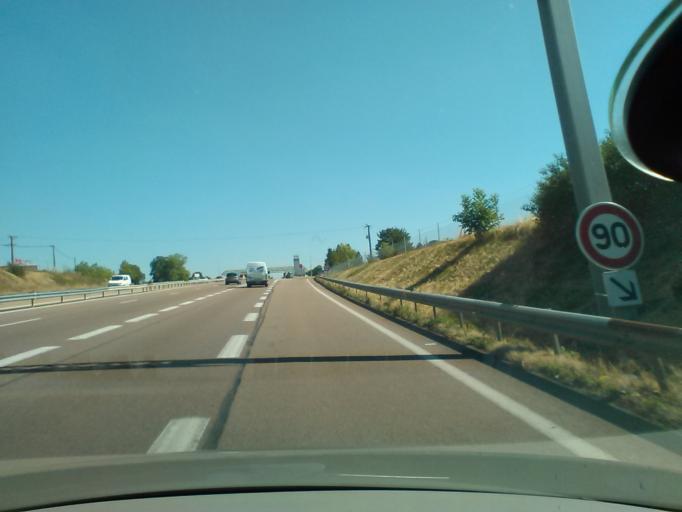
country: FR
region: Bourgogne
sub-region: Departement de l'Yonne
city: Venoy
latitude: 47.7920
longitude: 3.6676
